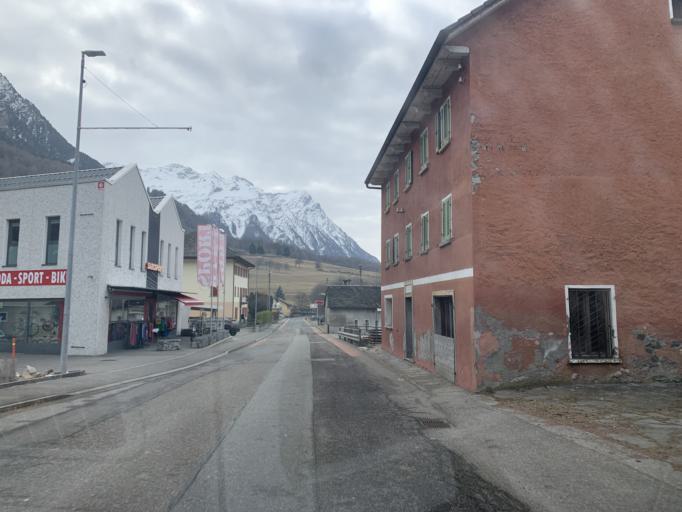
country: CH
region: Ticino
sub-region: Blenio District
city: Acquarossa
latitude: 46.5274
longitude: 8.9399
